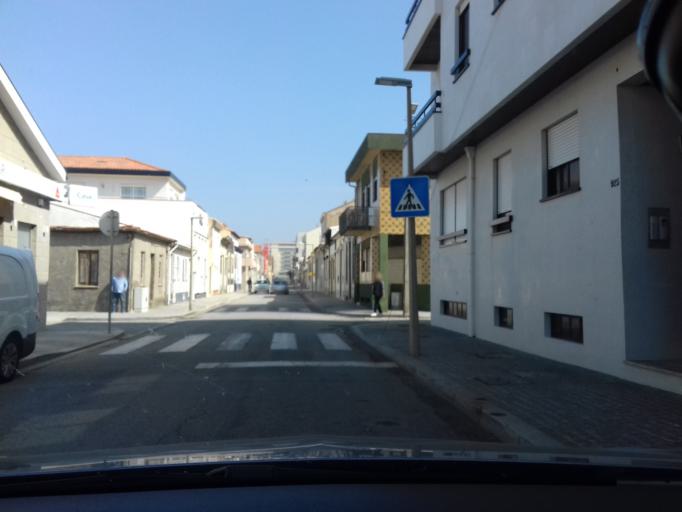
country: PT
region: Aveiro
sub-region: Espinho
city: Espinho
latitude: 41.0052
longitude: -8.6454
